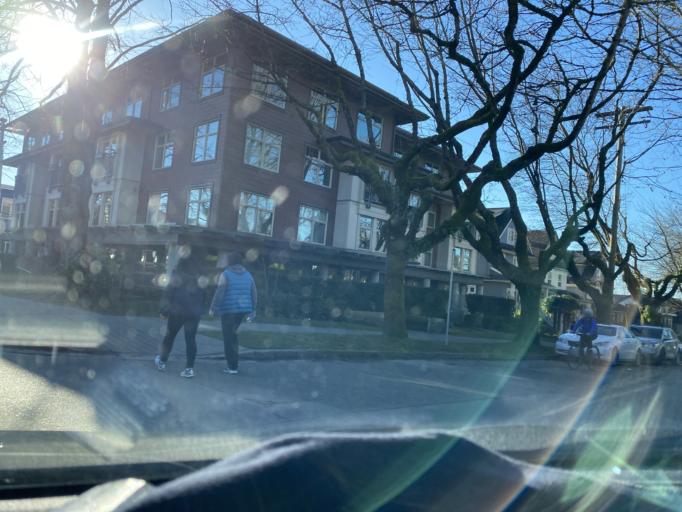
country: CA
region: British Columbia
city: West End
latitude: 49.2649
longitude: -123.1577
